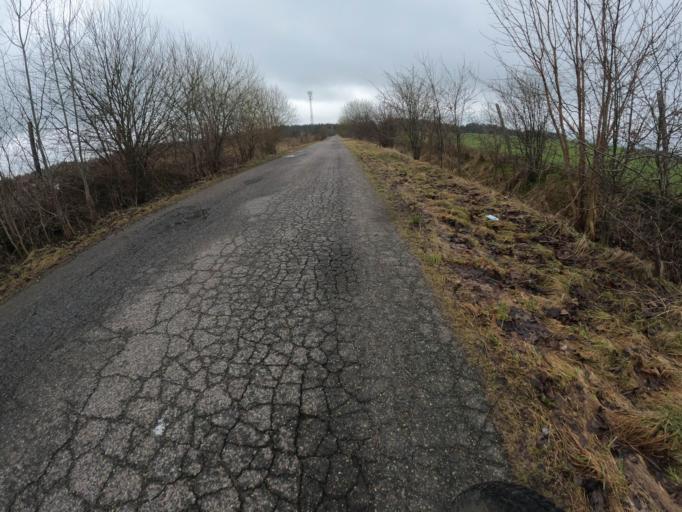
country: PL
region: West Pomeranian Voivodeship
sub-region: Powiat slawienski
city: Slawno
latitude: 54.2664
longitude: 16.6712
